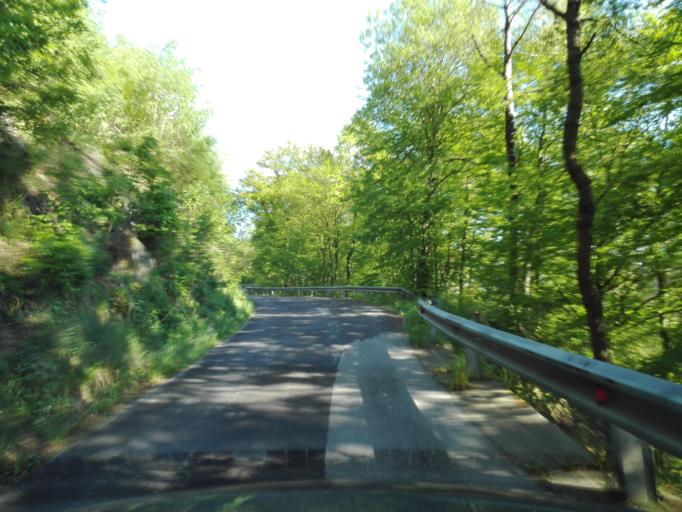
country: AT
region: Upper Austria
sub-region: Politischer Bezirk Rohrbach
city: Pfarrkirchen im Muehlkreis
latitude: 48.4619
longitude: 13.8163
